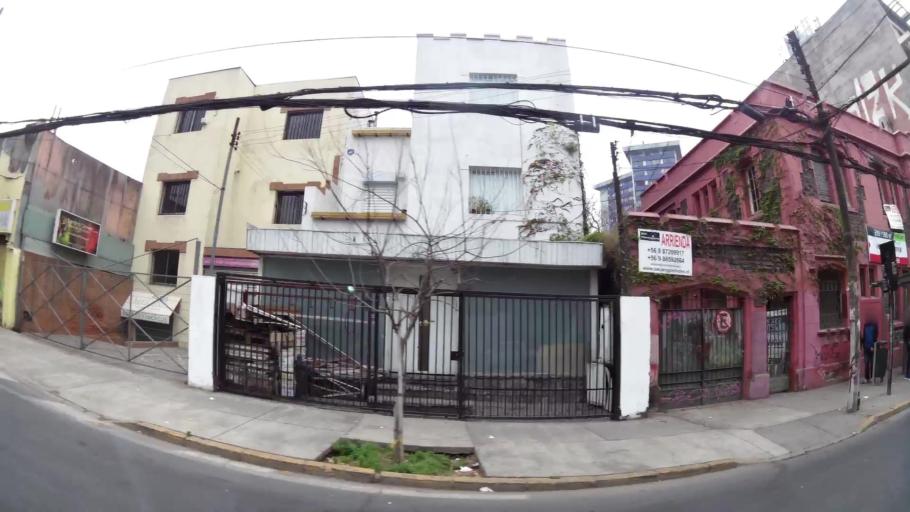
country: CL
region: Santiago Metropolitan
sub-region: Provincia de Santiago
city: Santiago
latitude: -33.4410
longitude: -70.6303
